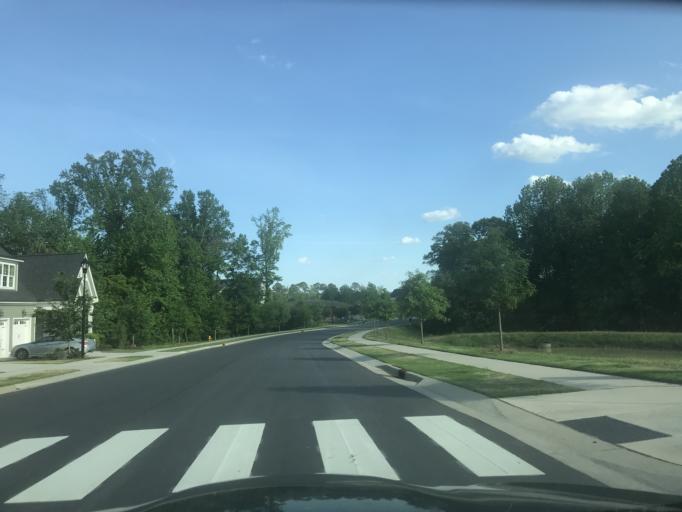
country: US
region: North Carolina
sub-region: Wake County
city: Knightdale
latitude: 35.7693
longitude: -78.4315
